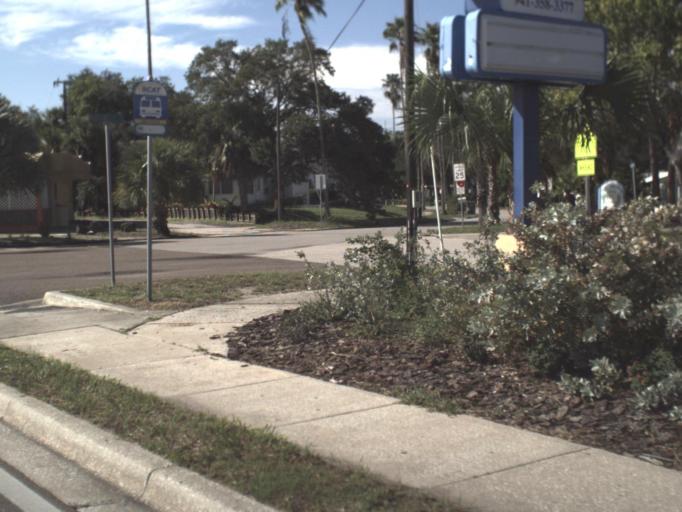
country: US
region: Florida
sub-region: Sarasota County
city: Sarasota
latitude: 27.3632
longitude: -82.5504
